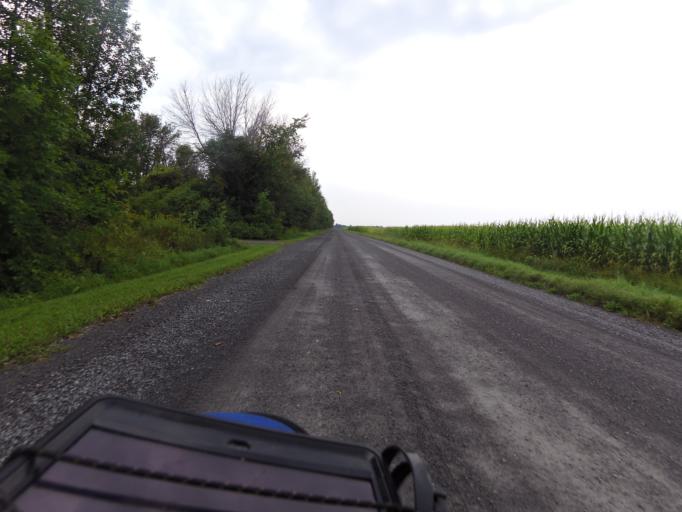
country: CA
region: Ontario
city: Ottawa
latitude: 45.1696
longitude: -75.4262
